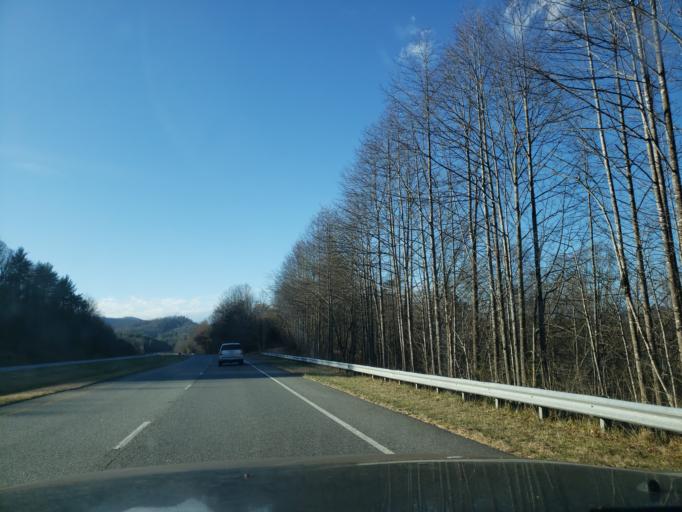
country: US
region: North Carolina
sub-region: Wilkes County
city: Millers Creek
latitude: 36.1509
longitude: -81.3268
